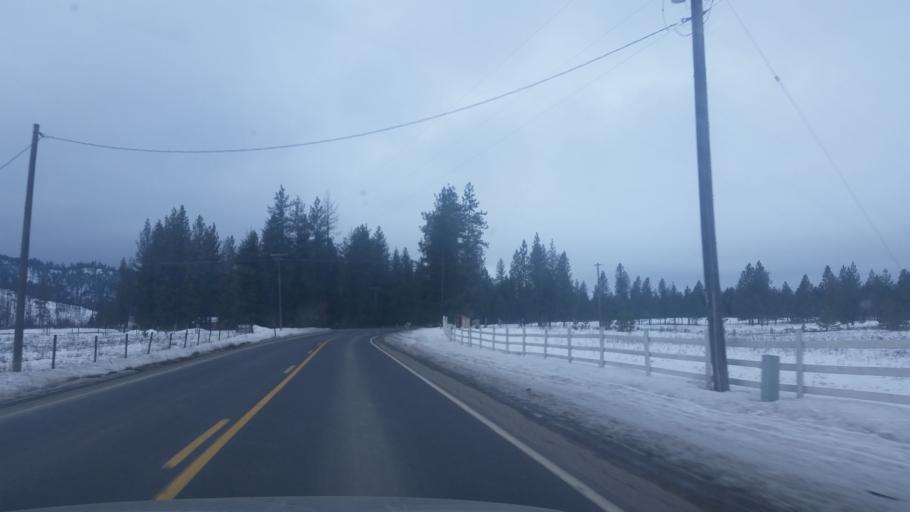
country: US
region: Washington
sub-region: Spokane County
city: Deer Park
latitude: 47.9632
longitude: -117.7454
